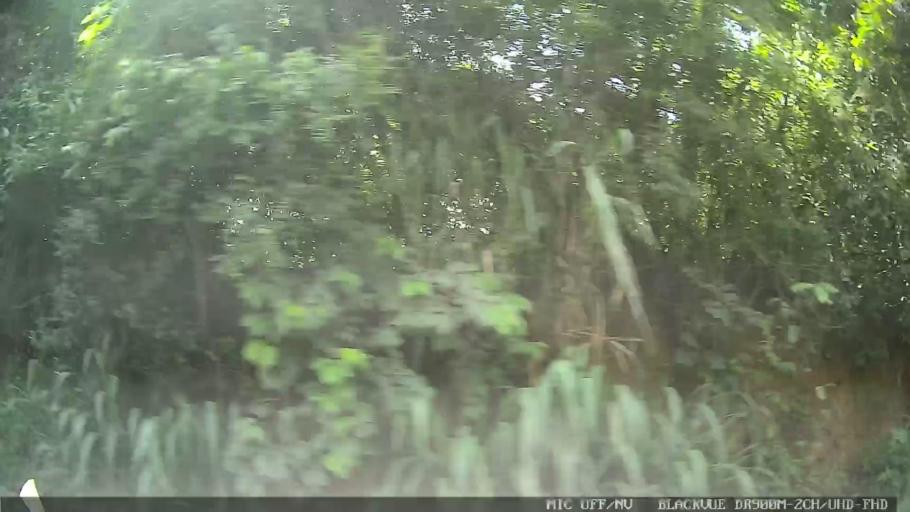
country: BR
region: Sao Paulo
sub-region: Suzano
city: Suzano
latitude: -23.4918
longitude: -46.2888
